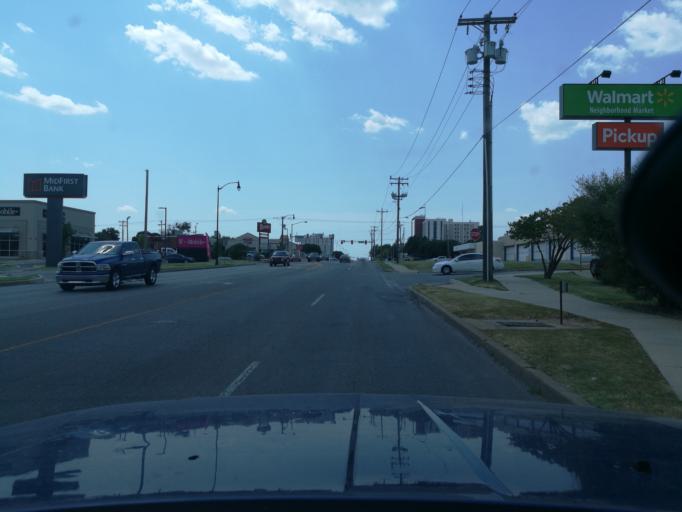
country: US
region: Oklahoma
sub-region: Oklahoma County
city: Oklahoma City
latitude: 35.4208
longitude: -97.5286
